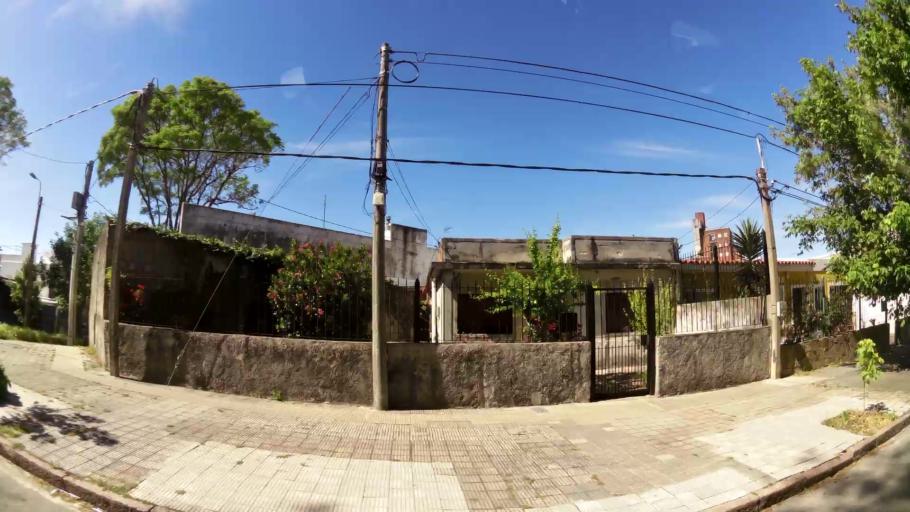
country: UY
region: Montevideo
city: Montevideo
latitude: -34.8878
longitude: -56.1316
